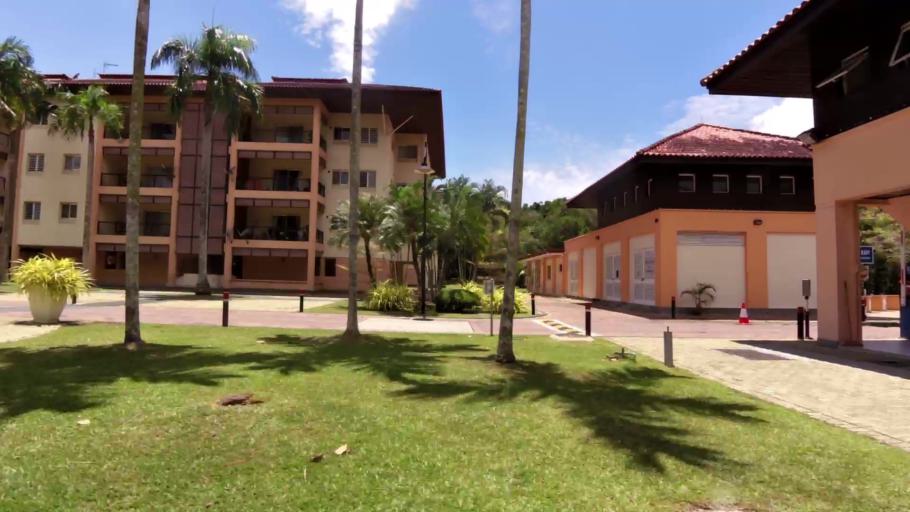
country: BN
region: Brunei and Muara
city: Bandar Seri Begawan
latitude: 4.9521
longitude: 114.8941
